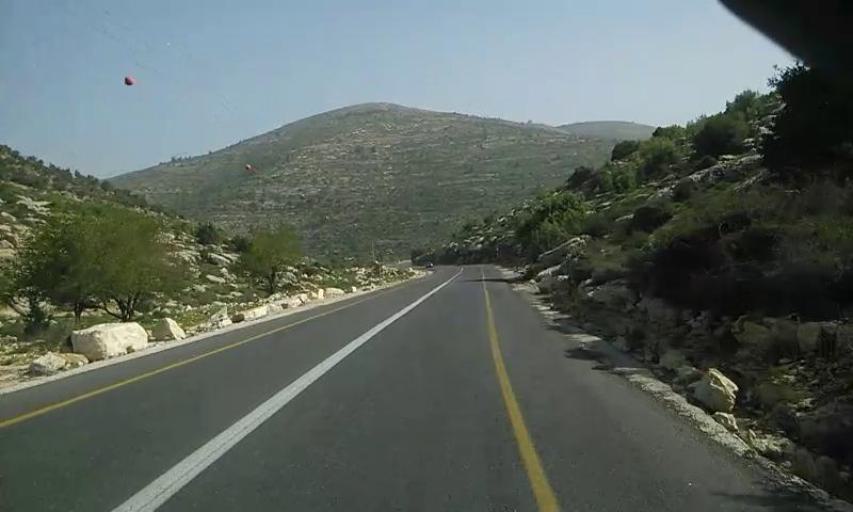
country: PS
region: West Bank
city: `Atarah
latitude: 32.0007
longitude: 35.2261
